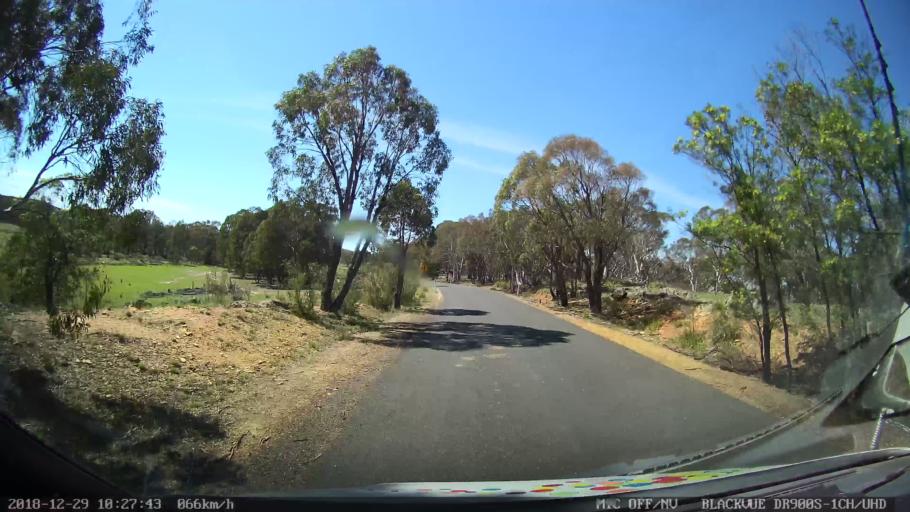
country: AU
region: New South Wales
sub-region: Yass Valley
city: Gundaroo
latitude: -34.9368
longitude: 149.4515
